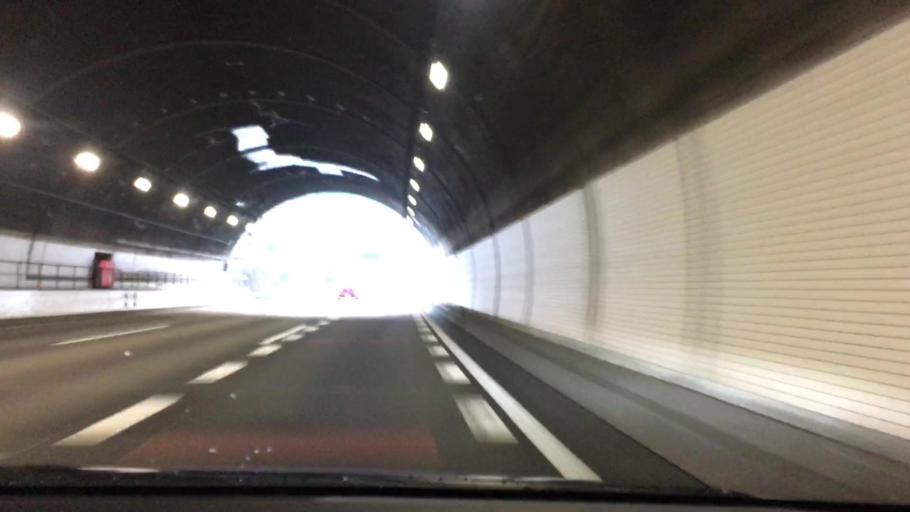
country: JP
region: Shizuoka
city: Gotemba
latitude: 35.3606
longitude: 139.0301
